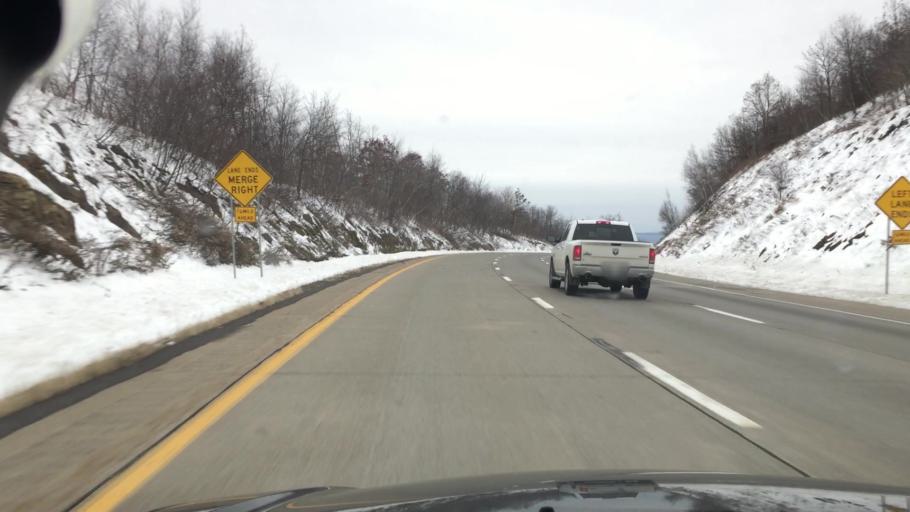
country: US
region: Pennsylvania
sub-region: Luzerne County
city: Harleigh
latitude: 41.0629
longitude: -75.9890
